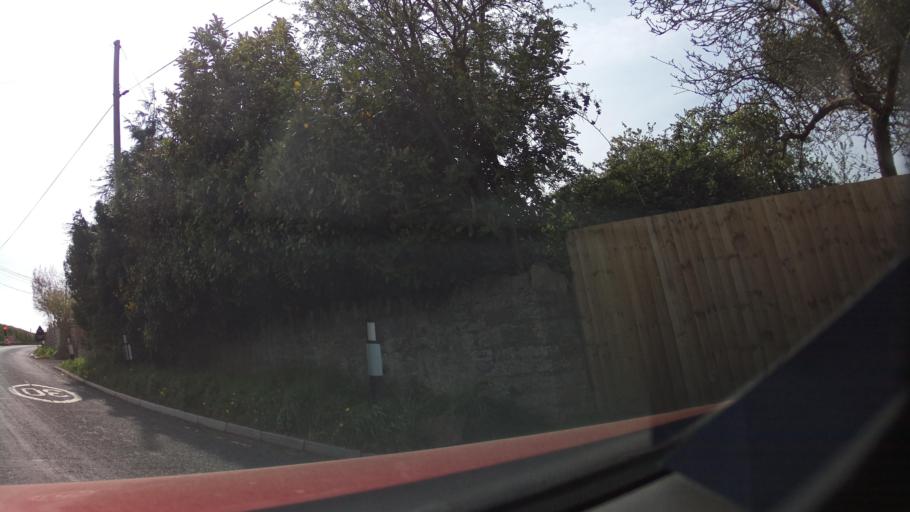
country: GB
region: England
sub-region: Somerset
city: Street
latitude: 51.1211
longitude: -2.7959
